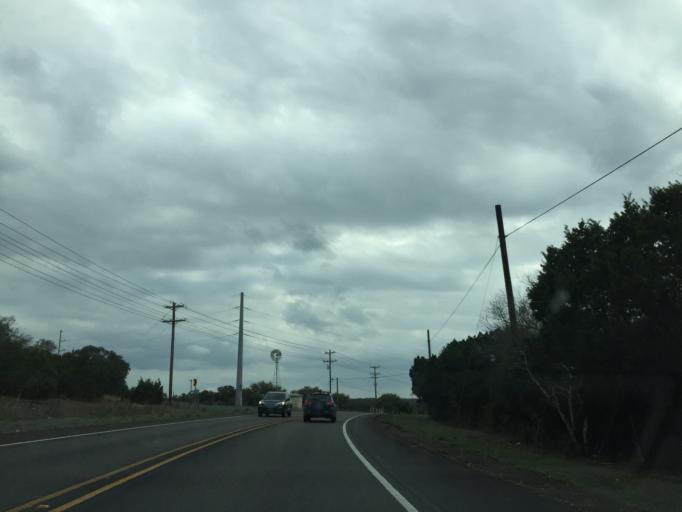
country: US
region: Texas
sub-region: Travis County
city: Shady Hollow
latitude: 30.1762
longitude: -97.9289
